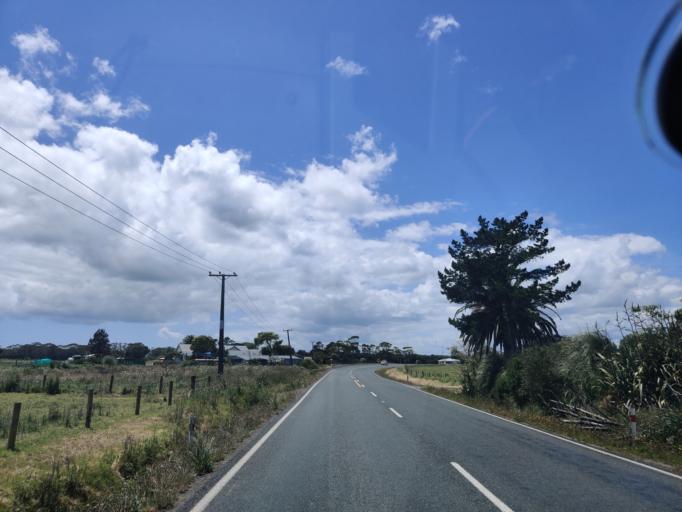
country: NZ
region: Northland
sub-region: Far North District
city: Kaitaia
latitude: -35.0259
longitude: 173.2479
